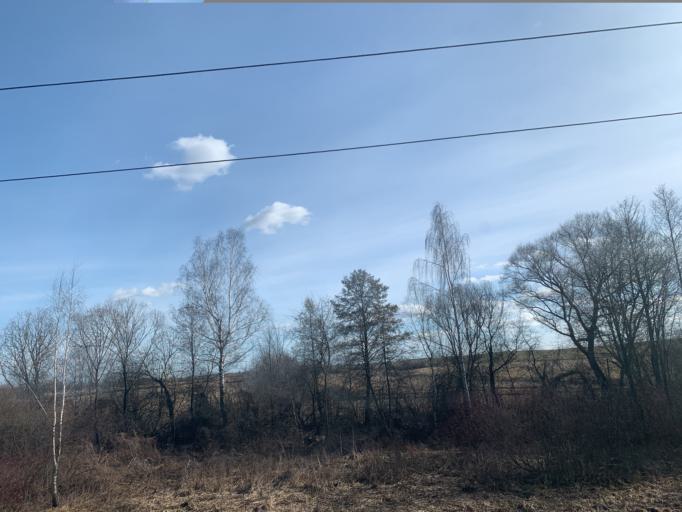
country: BY
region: Minsk
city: Stan'kava
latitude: 53.6838
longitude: 27.2156
